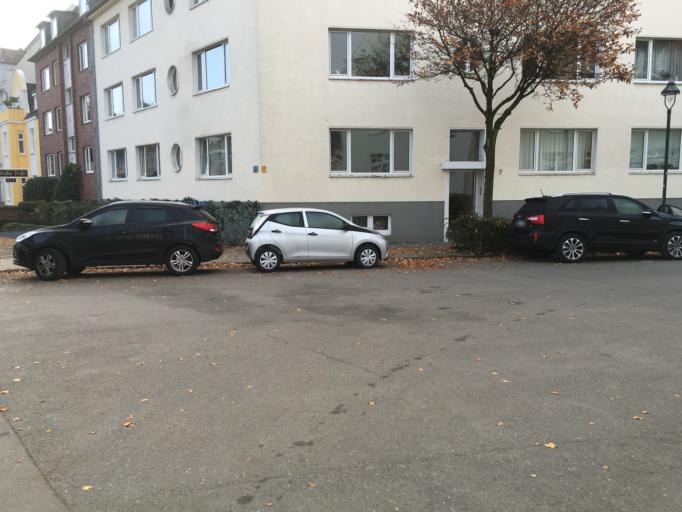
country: DE
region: North Rhine-Westphalia
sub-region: Regierungsbezirk Dusseldorf
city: Erkrath
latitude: 51.2383
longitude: 6.8535
